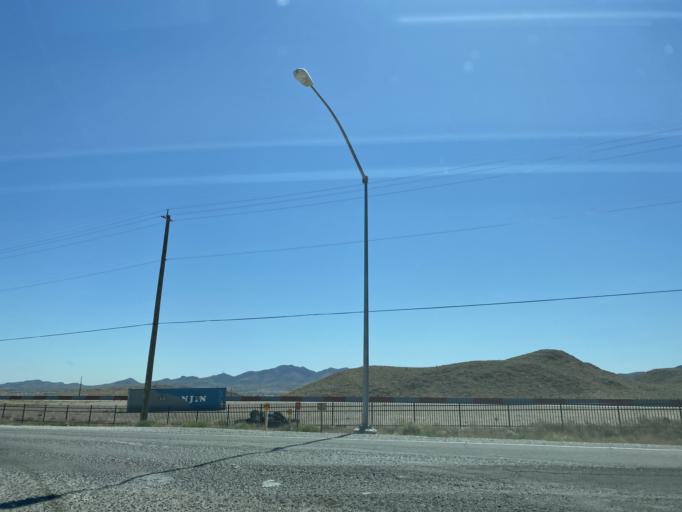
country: US
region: Nevada
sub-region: Clark County
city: Enterprise
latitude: 35.9301
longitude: -115.1922
